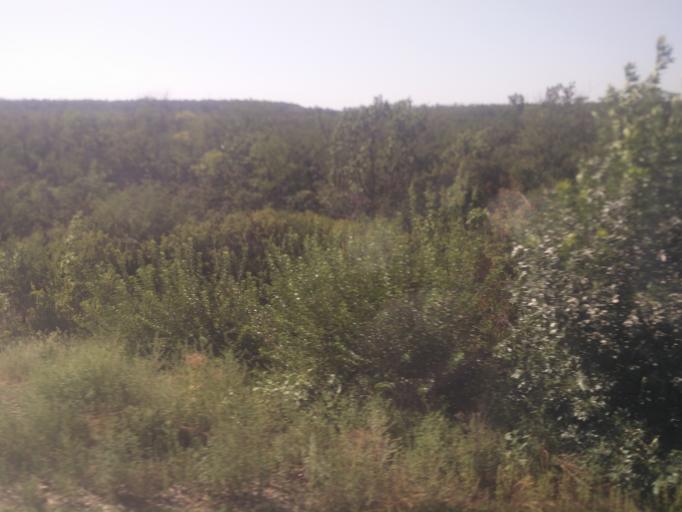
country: RU
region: Rostov
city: Gornyy
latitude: 47.8794
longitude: 40.1531
